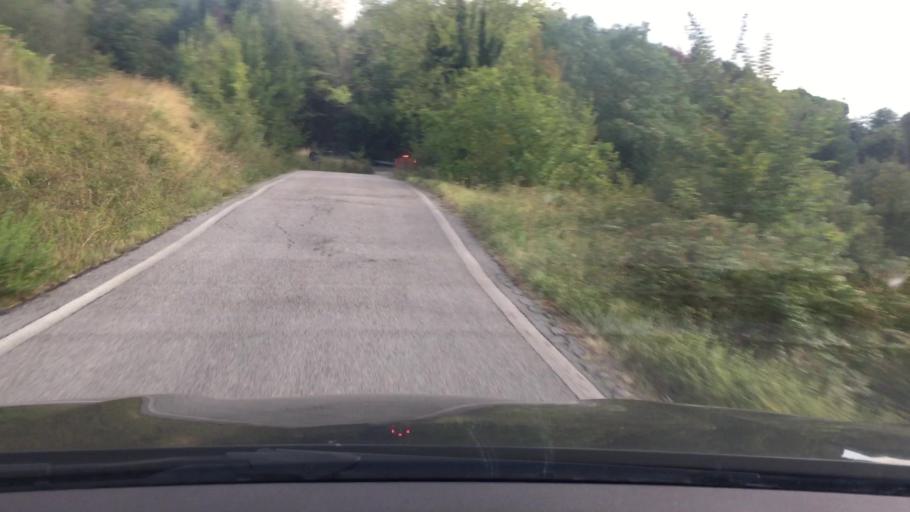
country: IT
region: Emilia-Romagna
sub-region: Provincia di Ravenna
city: Brisighella
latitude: 44.2034
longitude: 11.7765
